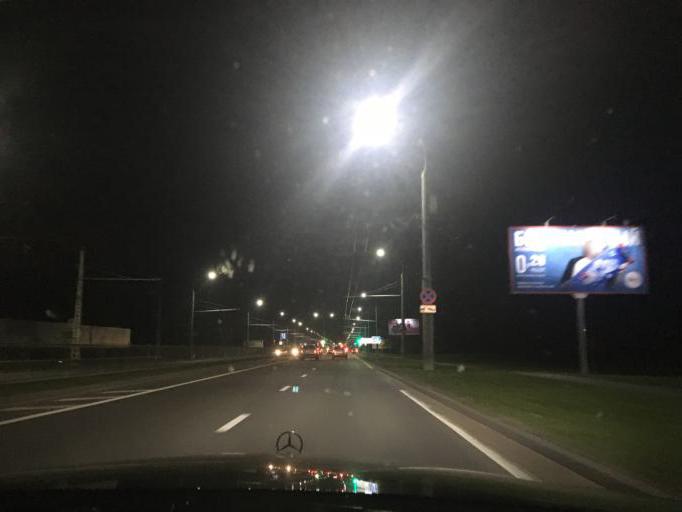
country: BY
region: Brest
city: Brest
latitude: 52.1049
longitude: 23.7909
